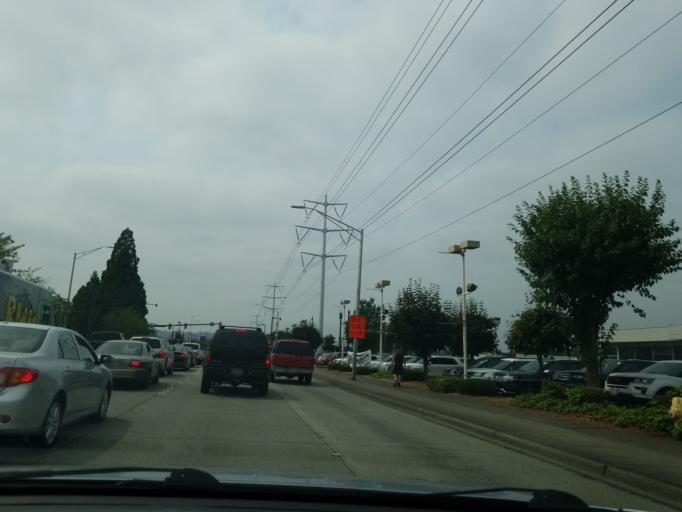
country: US
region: Washington
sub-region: King County
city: Renton
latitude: 47.4710
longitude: -122.2158
